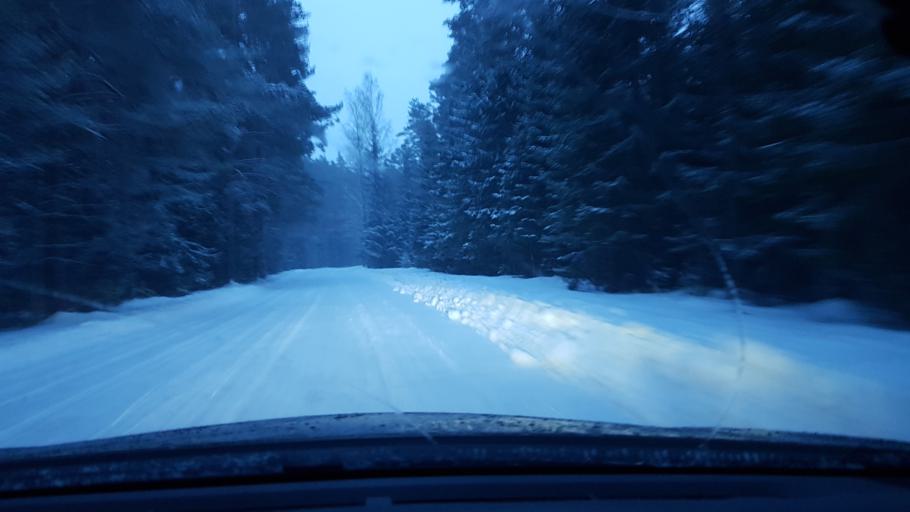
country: EE
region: Harju
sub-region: Kuusalu vald
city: Kuusalu
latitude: 59.5168
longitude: 25.5622
